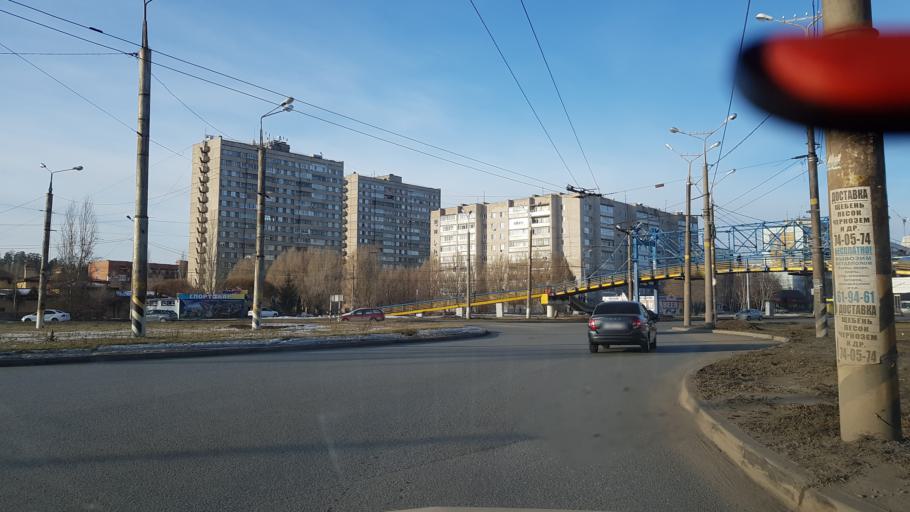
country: RU
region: Samara
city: Tol'yatti
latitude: 53.5293
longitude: 49.3973
